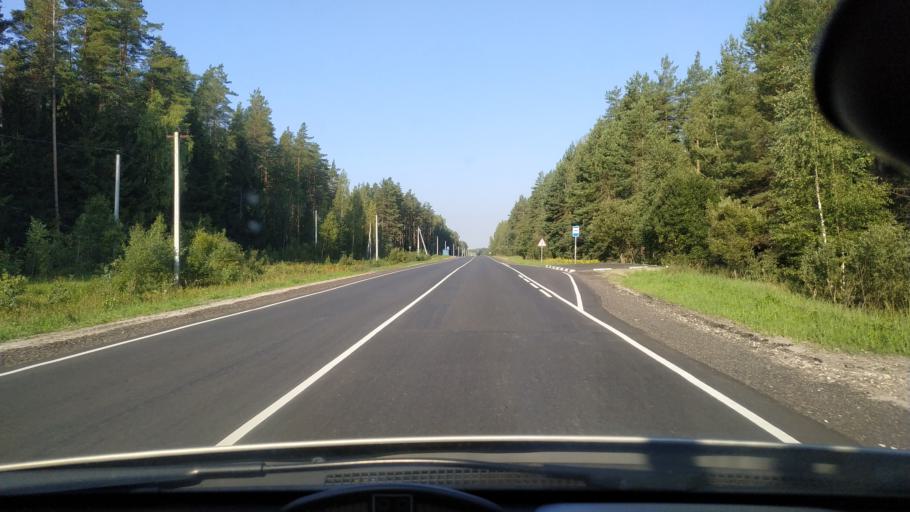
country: RU
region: Moskovskaya
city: Misheronskiy
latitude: 55.6578
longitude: 39.7881
